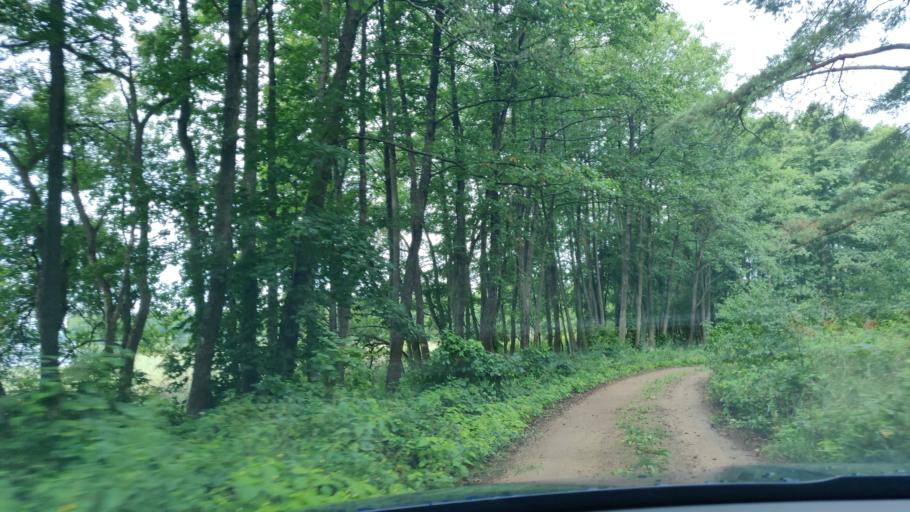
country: LT
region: Vilnius County
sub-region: Trakai
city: Rudiskes
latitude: 54.6098
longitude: 24.8248
